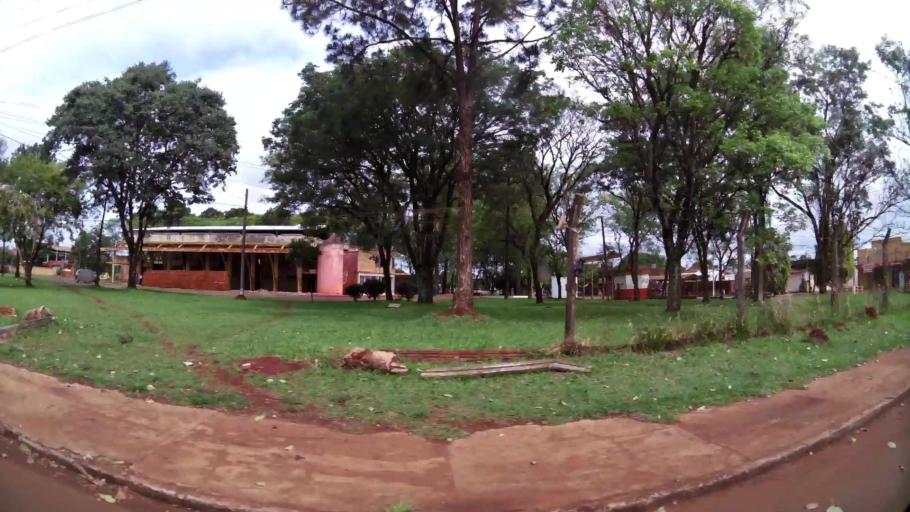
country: PY
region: Alto Parana
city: Ciudad del Este
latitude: -25.3888
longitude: -54.6461
